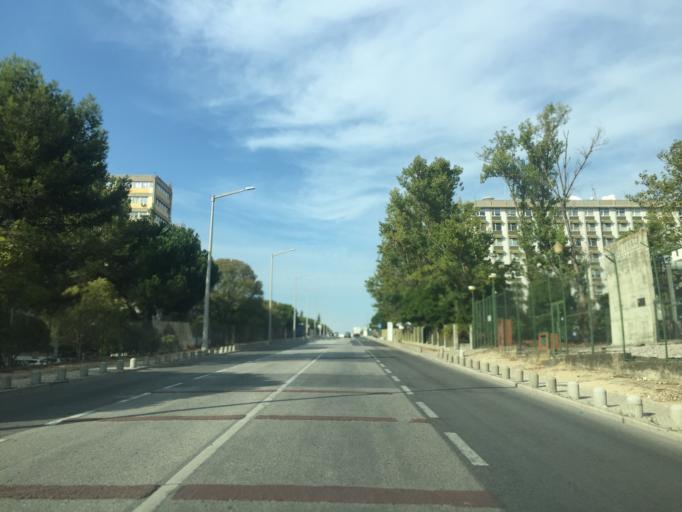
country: PT
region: Lisbon
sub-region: Loures
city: Moscavide
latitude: 38.7747
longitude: -9.1261
